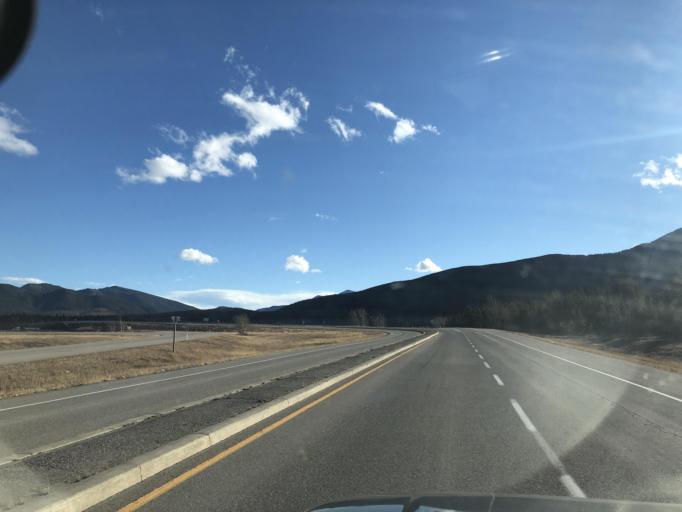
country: CA
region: Alberta
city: Canmore
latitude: 51.0816
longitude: -115.0620
